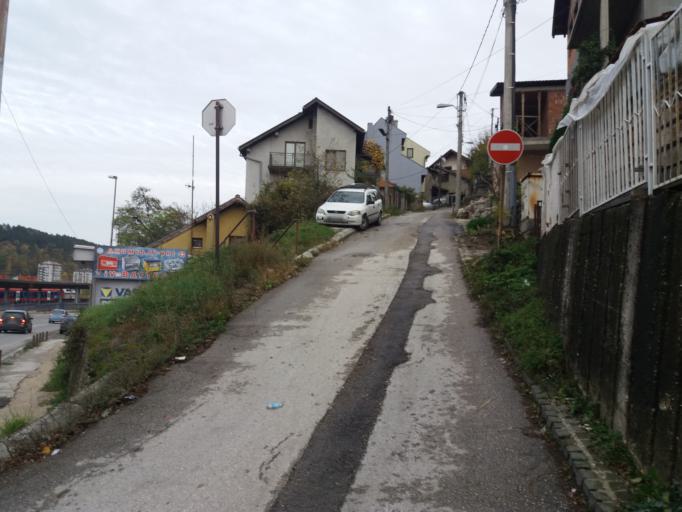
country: RS
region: Central Serbia
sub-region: Zlatiborski Okrug
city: Uzice
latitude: 43.8534
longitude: 19.8379
